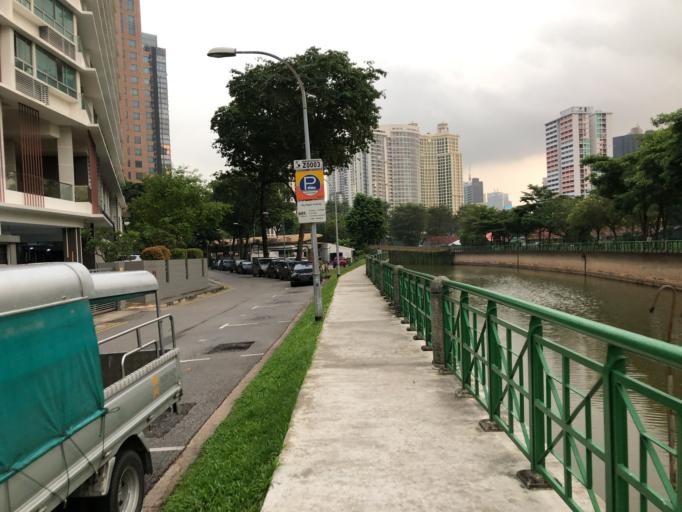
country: SG
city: Singapore
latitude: 1.2924
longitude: 103.8300
